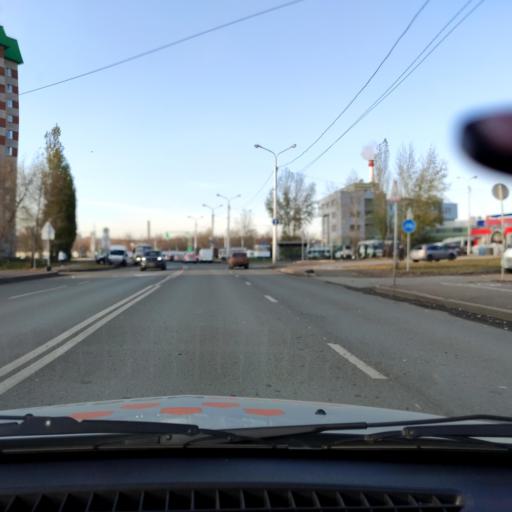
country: RU
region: Bashkortostan
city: Ufa
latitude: 54.7787
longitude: 56.0731
